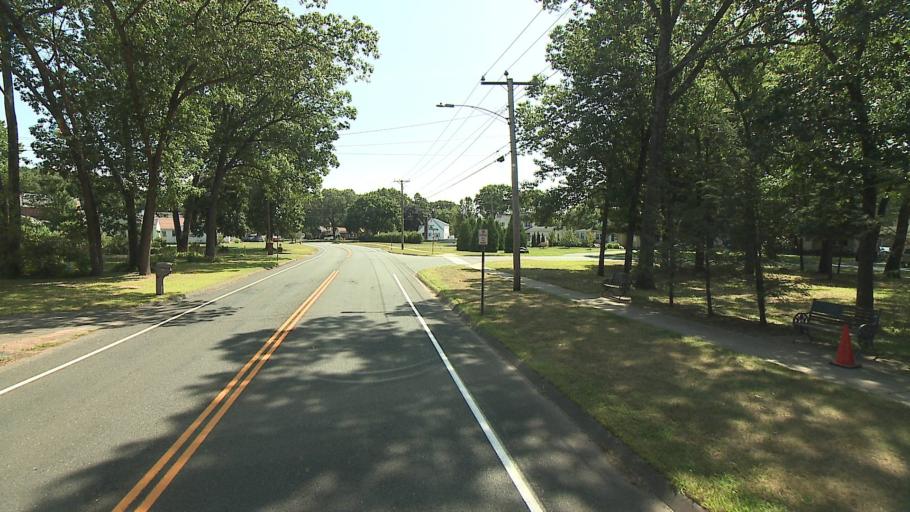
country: US
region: Connecticut
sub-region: Hartford County
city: Windsor Locks
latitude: 41.9271
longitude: -72.6626
